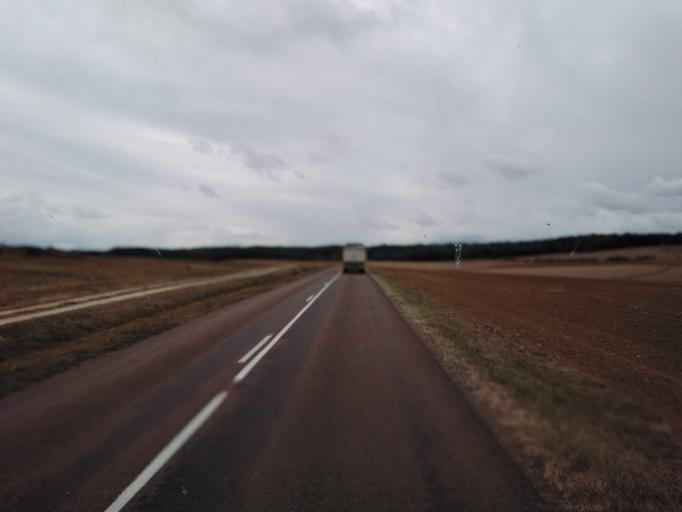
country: FR
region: Champagne-Ardenne
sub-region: Departement de l'Aube
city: Vendeuvre-sur-Barse
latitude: 48.2846
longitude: 4.5122
